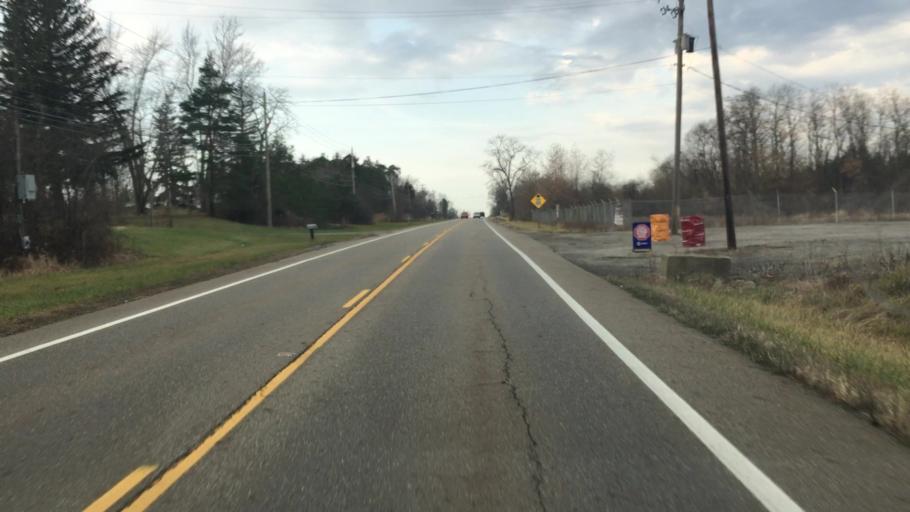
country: US
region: Ohio
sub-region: Mahoning County
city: Canfield
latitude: 41.0244
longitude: -80.8461
